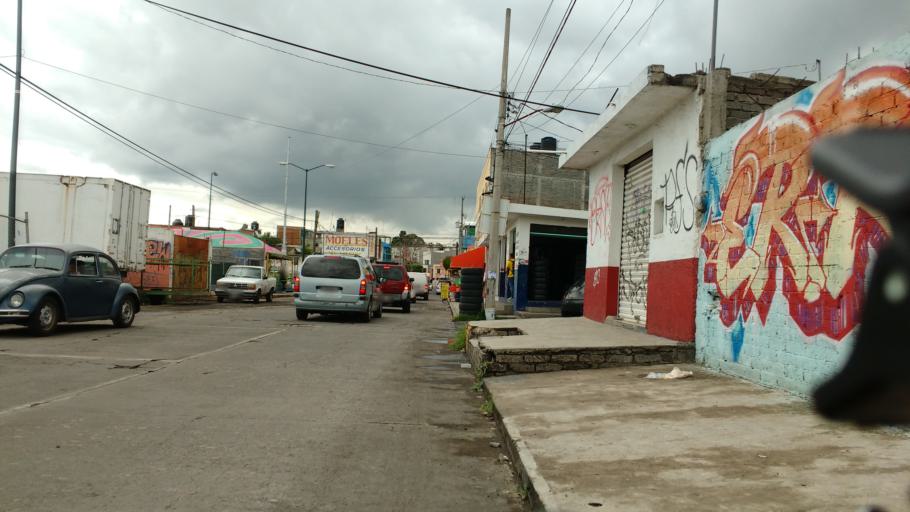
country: MX
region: Michoacan
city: Morelia
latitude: 19.7100
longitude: -101.2123
